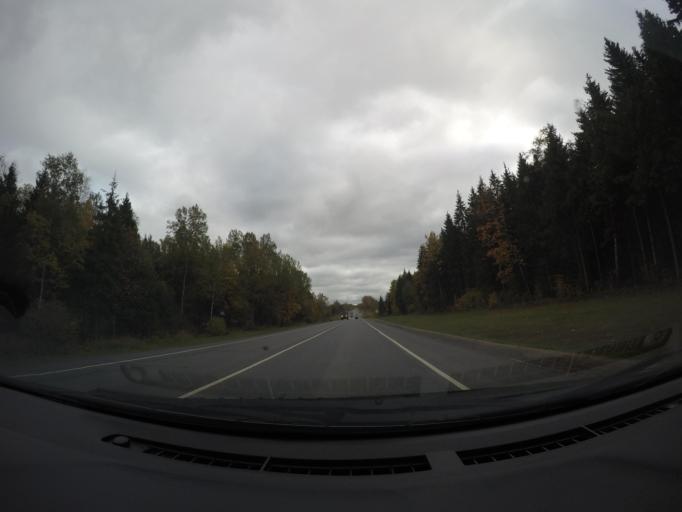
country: RU
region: Moskovskaya
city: Dorokhovo
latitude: 55.6009
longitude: 36.3586
